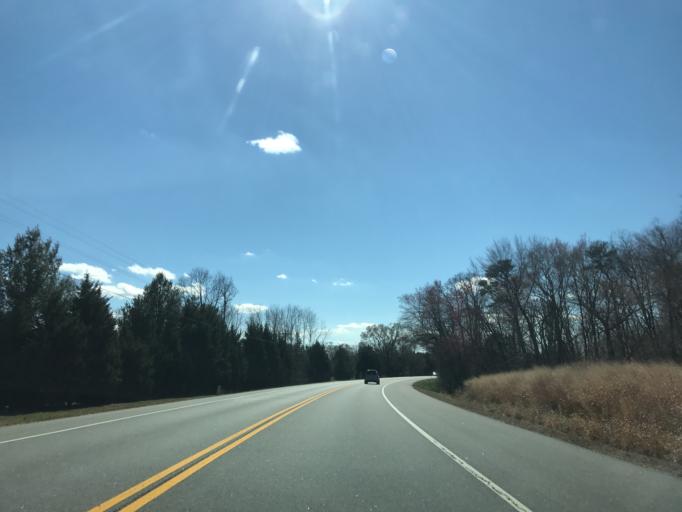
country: US
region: Maryland
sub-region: Queen Anne's County
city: Kingstown
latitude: 39.2386
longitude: -76.0324
